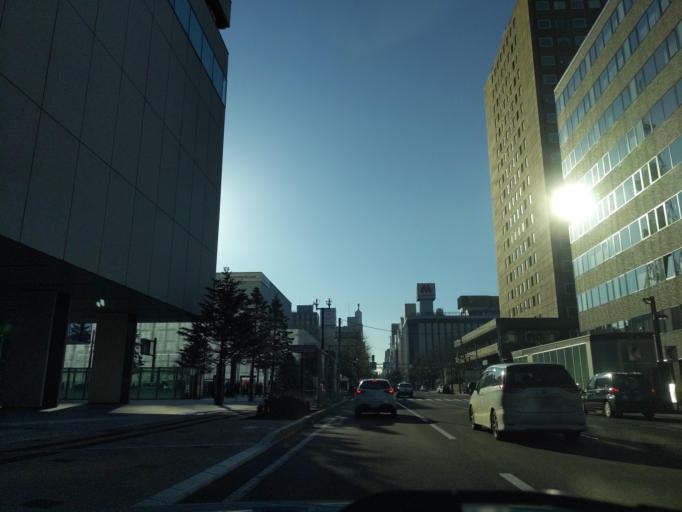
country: JP
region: Hokkaido
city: Sapporo
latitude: 43.0631
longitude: 141.3548
